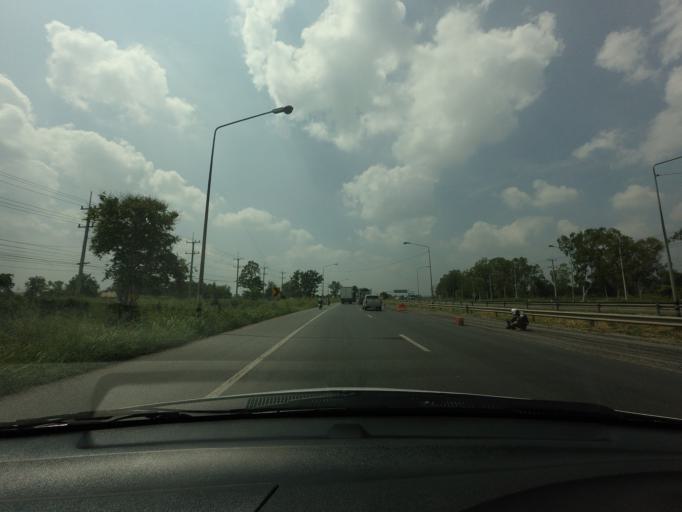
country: TH
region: Nakhon Ratchasima
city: Pak Chong
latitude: 14.6724
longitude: 101.4544
